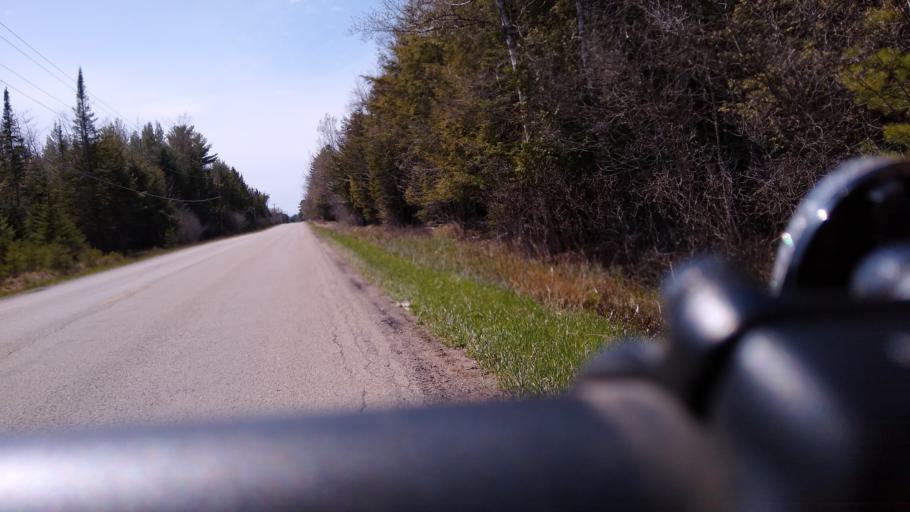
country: US
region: Michigan
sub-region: Delta County
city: Escanaba
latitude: 45.7353
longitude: -87.1740
